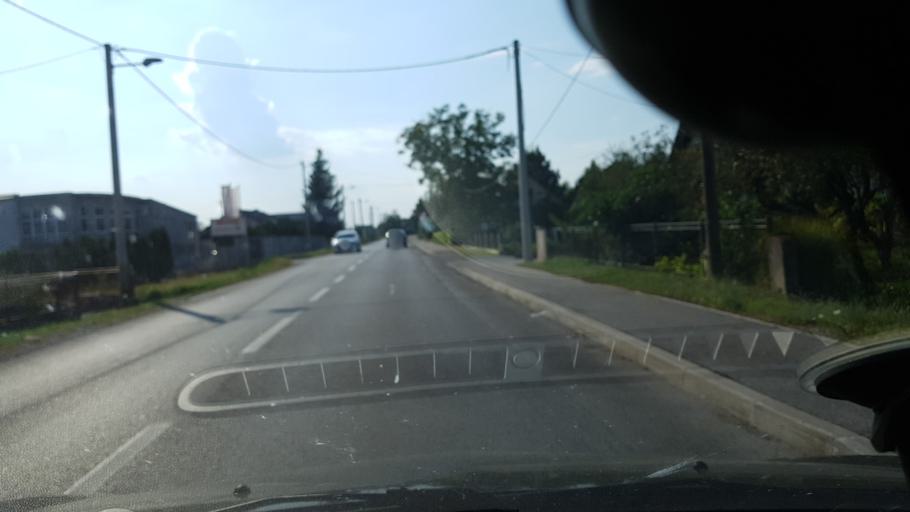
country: HR
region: Zagrebacka
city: Brdovec
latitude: 45.8793
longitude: 15.7298
